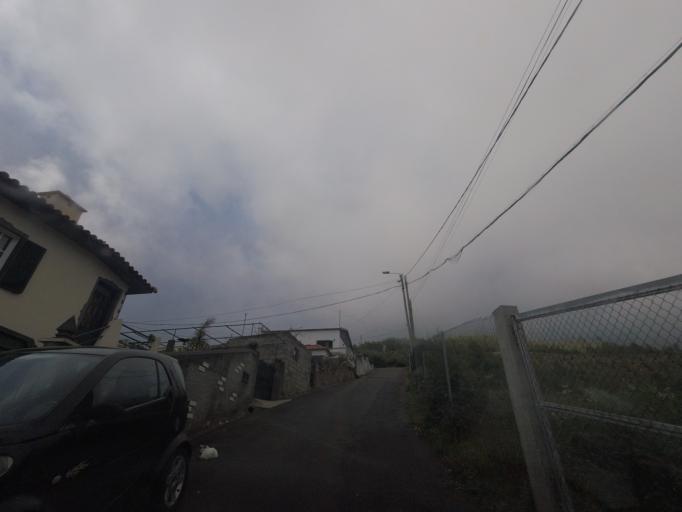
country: PT
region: Madeira
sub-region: Funchal
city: Nossa Senhora do Monte
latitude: 32.6821
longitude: -16.9084
